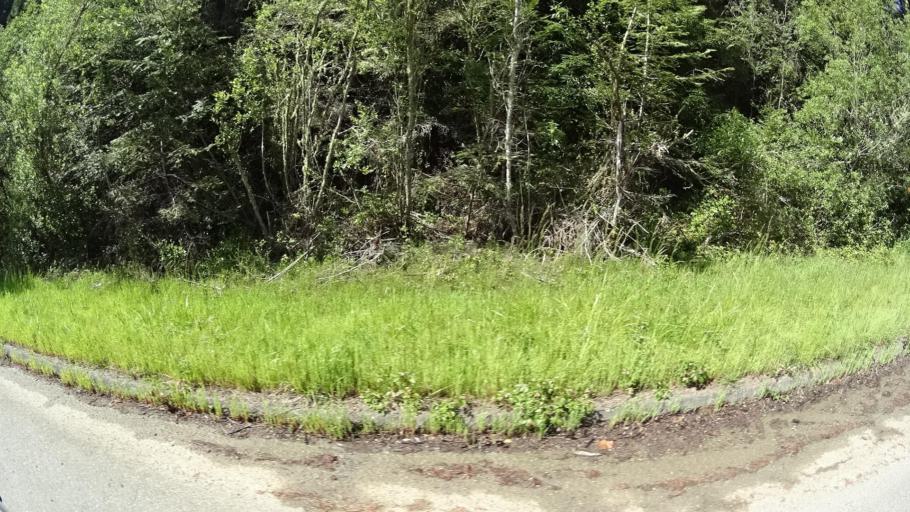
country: US
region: California
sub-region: Humboldt County
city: Hydesville
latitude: 40.5695
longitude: -124.1107
